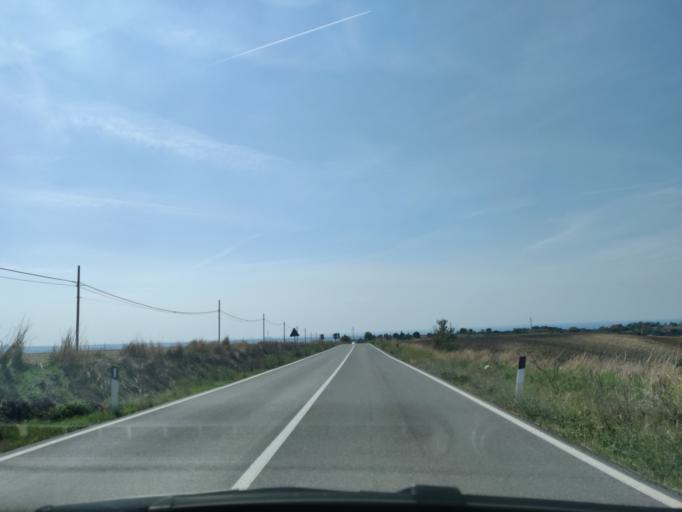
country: IT
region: Latium
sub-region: Provincia di Viterbo
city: Tarquinia
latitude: 42.2438
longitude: 11.8078
